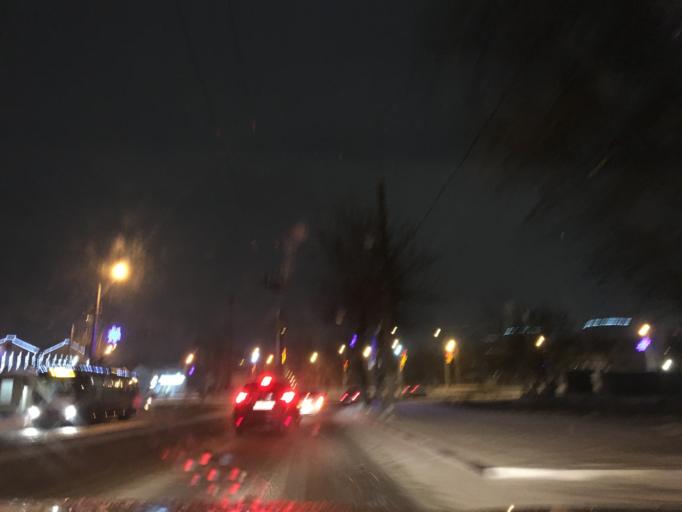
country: RU
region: Tula
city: Tula
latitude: 54.1845
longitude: 37.5725
